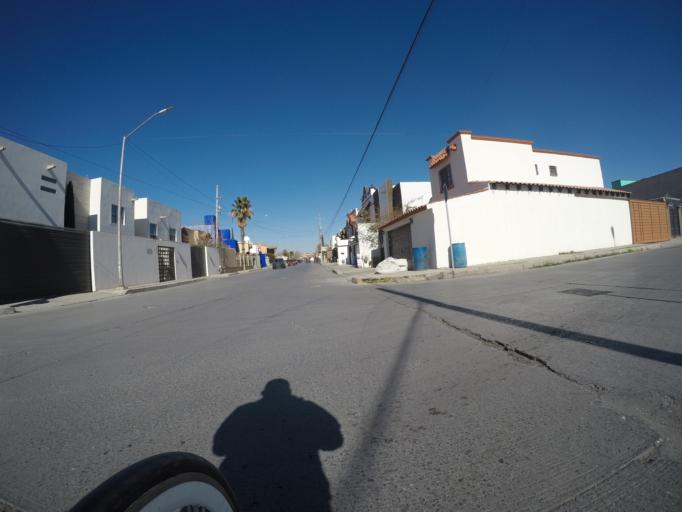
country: MX
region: Chihuahua
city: Ciudad Juarez
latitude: 31.7036
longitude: -106.4133
